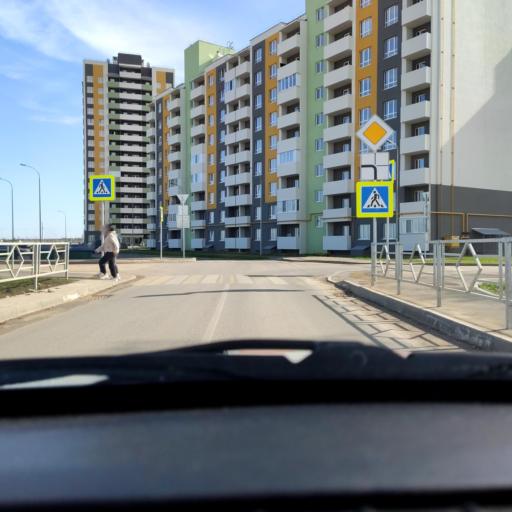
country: RU
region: Samara
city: Samara
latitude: 53.1001
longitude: 50.1707
